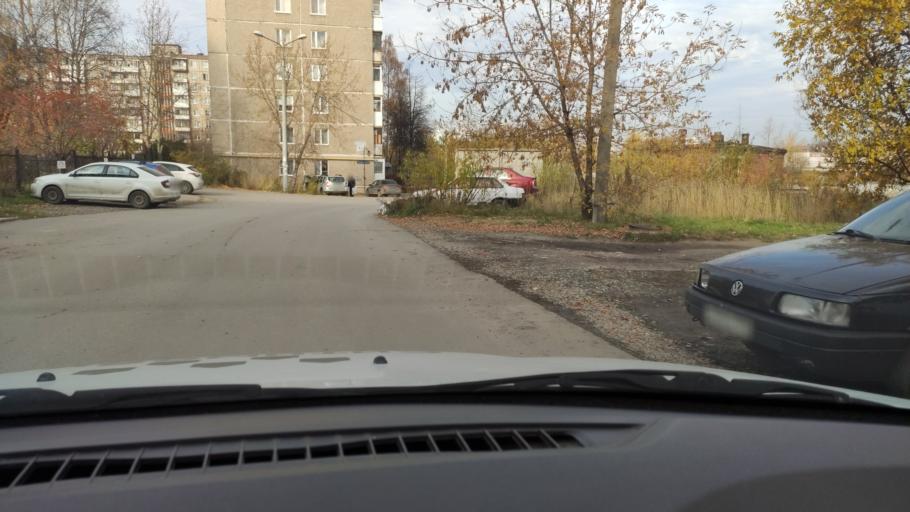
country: RU
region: Perm
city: Perm
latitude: 57.9788
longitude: 56.2816
